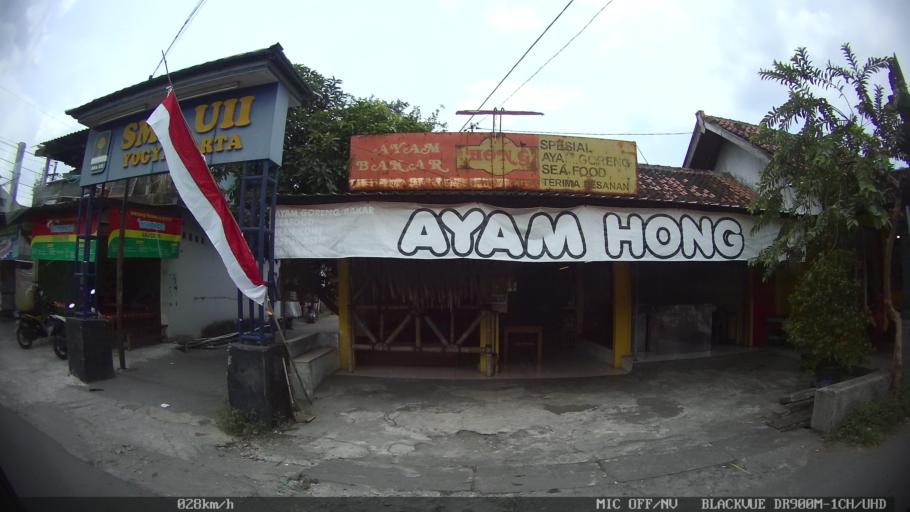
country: ID
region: Daerah Istimewa Yogyakarta
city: Yogyakarta
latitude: -7.7886
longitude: 110.3987
